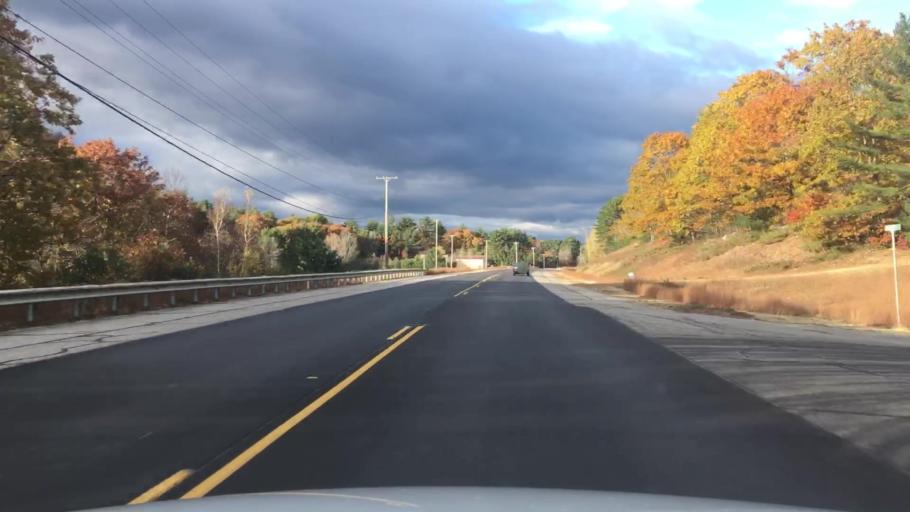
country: US
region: Maine
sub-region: Androscoggin County
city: Livermore
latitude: 44.3548
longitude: -70.2566
